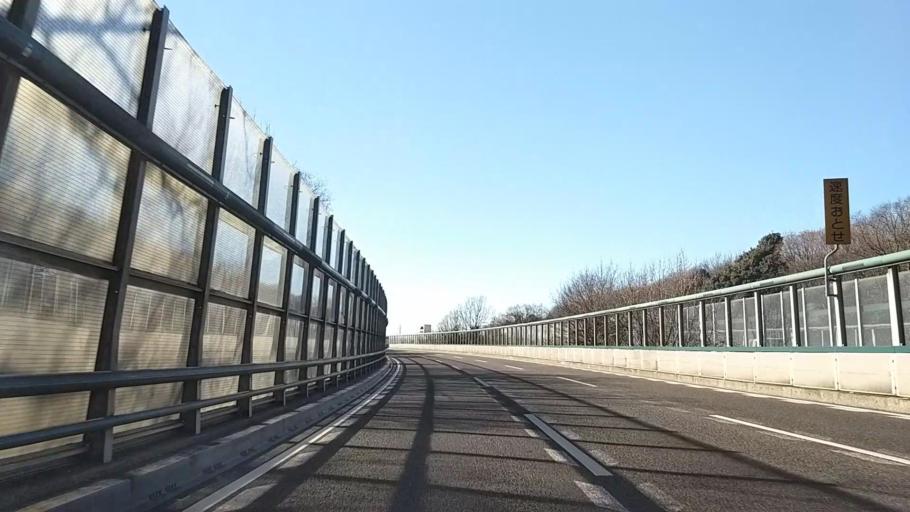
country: JP
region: Kanagawa
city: Yokohama
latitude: 35.4684
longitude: 139.5674
